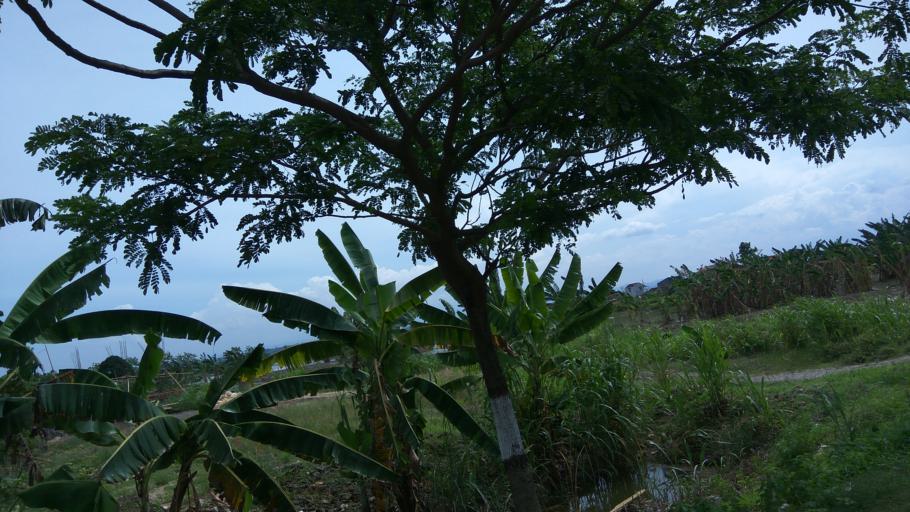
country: ID
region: Central Java
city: Mranggen
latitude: -7.0510
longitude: 110.6496
